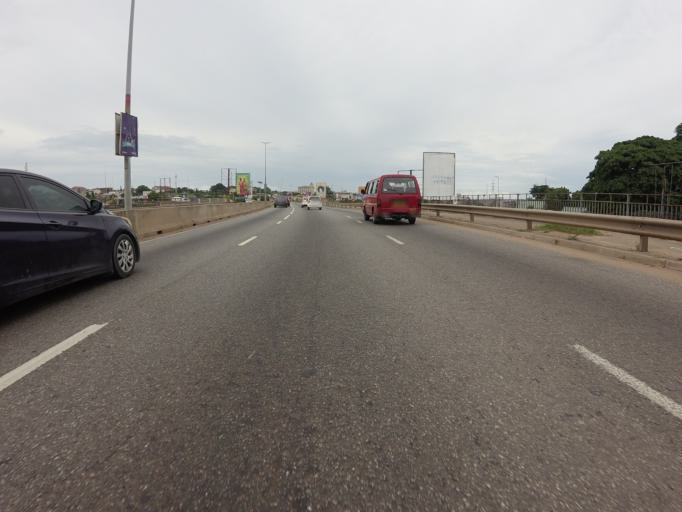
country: GH
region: Greater Accra
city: Accra
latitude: 5.5898
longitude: -0.2188
